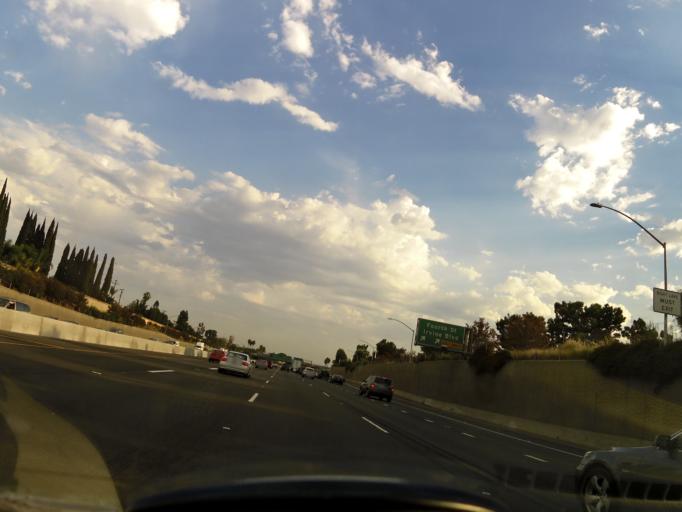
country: US
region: California
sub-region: Orange County
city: Tustin
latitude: 33.7534
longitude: -117.8318
